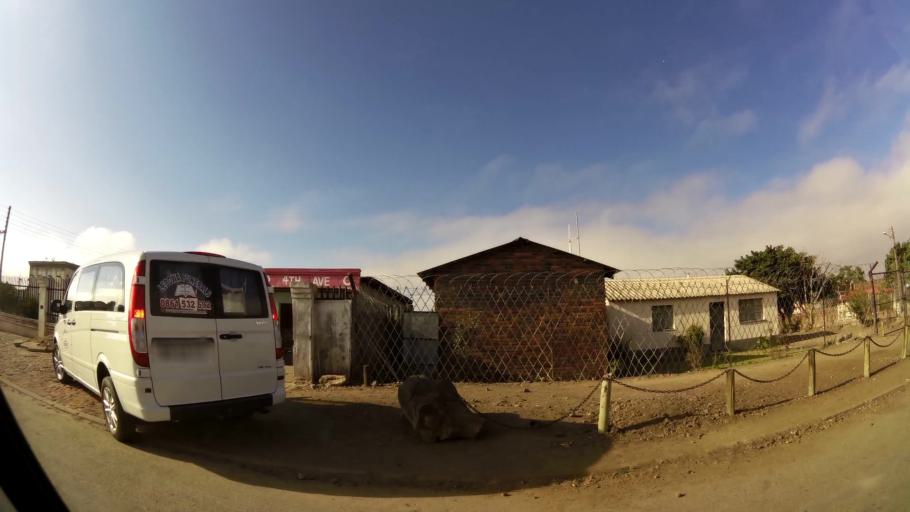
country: ZA
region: Limpopo
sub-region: Capricorn District Municipality
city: Polokwane
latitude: -23.8436
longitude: 29.3918
